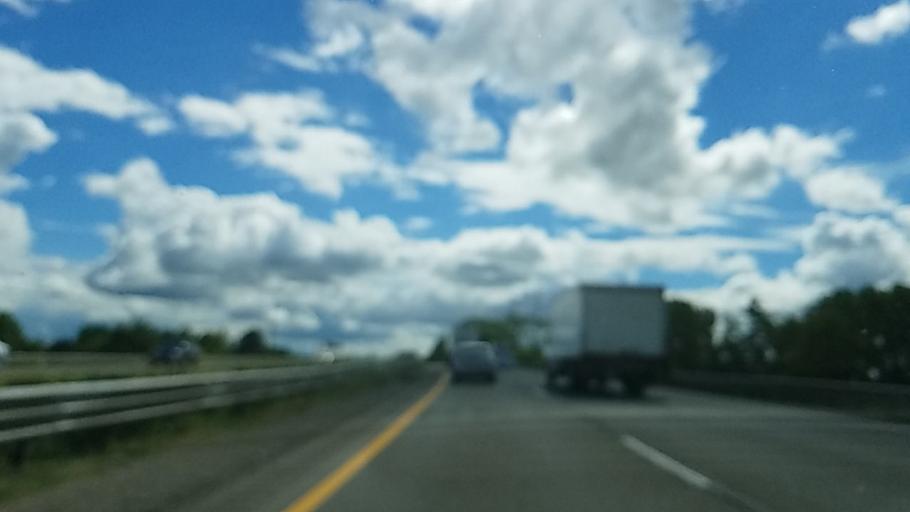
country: US
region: Michigan
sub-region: Livingston County
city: Whitmore Lake
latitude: 42.4268
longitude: -83.7681
